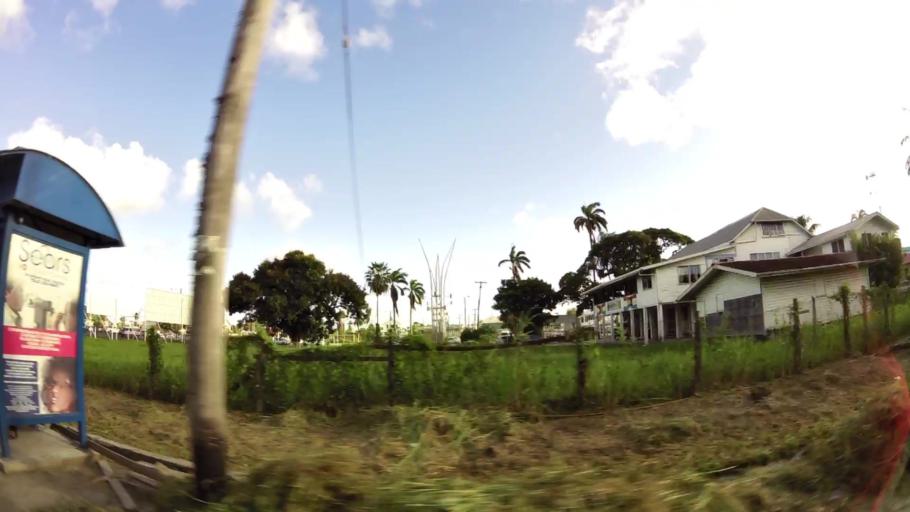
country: GY
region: Demerara-Mahaica
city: Georgetown
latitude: 6.8059
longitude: -58.1515
